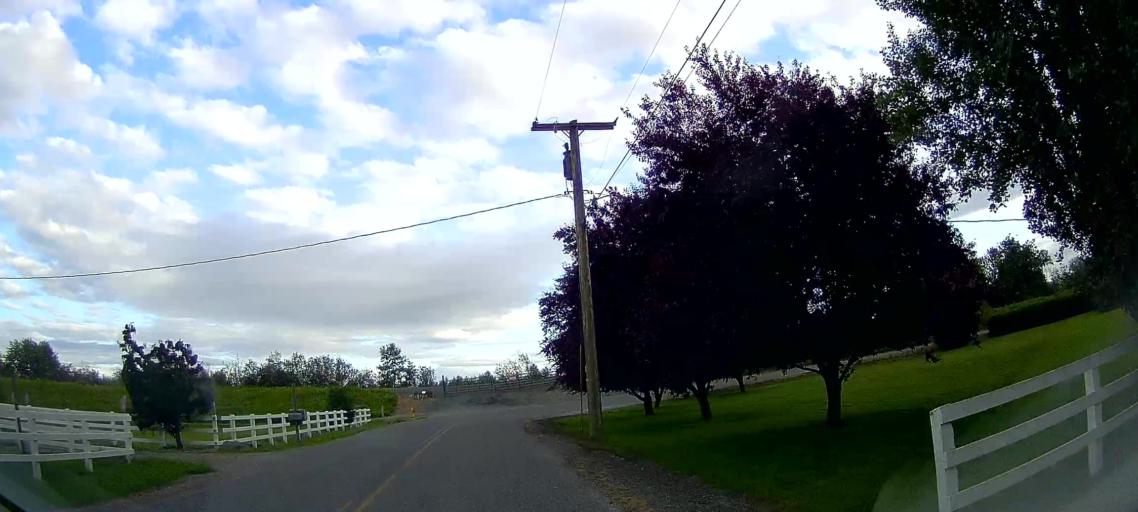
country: US
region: Washington
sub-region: Skagit County
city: Mount Vernon
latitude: 48.3696
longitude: -122.4005
